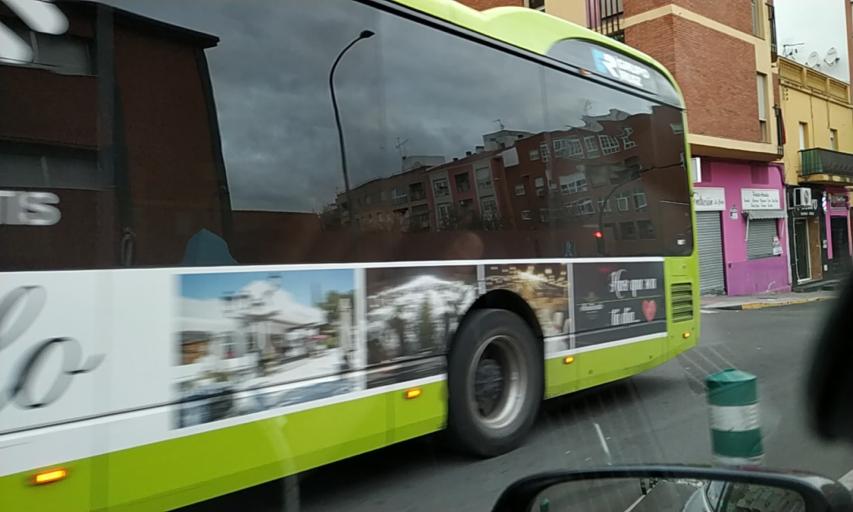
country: ES
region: Extremadura
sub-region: Provincia de Badajoz
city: Badajoz
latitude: 38.8757
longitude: -6.9555
